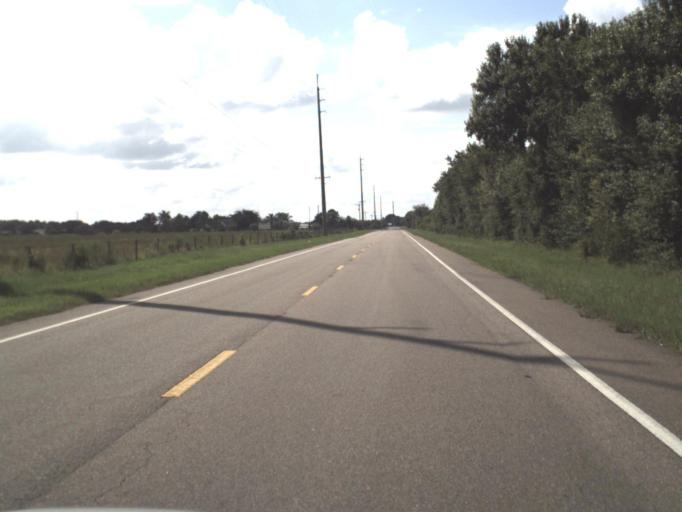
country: US
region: Florida
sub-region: Hardee County
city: Wauchula
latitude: 27.4852
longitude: -82.0019
